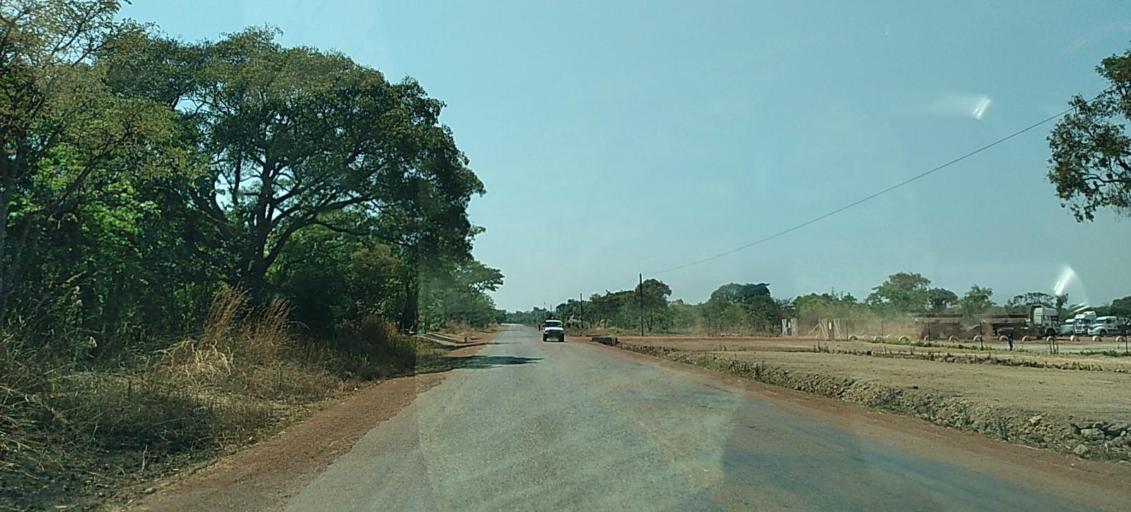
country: ZM
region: North-Western
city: Solwezi
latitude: -12.3570
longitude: 25.9294
